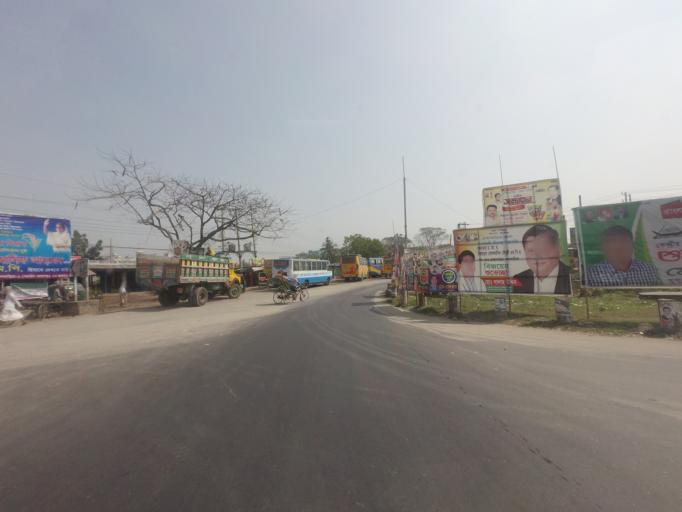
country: BD
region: Dhaka
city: Bhairab Bazar
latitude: 24.0385
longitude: 91.0034
